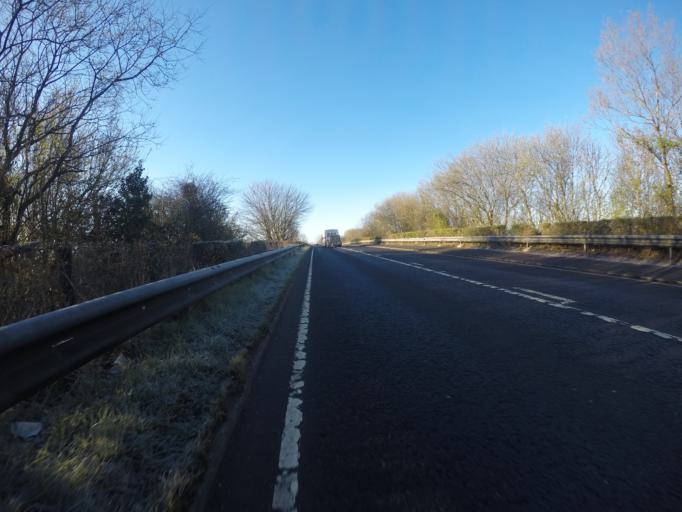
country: GB
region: Scotland
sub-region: North Ayrshire
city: Stevenston
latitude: 55.6377
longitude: -4.7402
